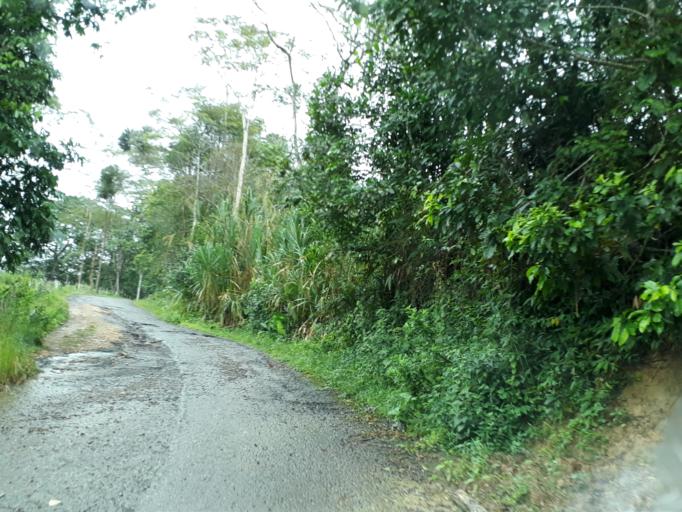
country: CO
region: Boyaca
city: Santa Maria
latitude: 4.6950
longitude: -73.3048
